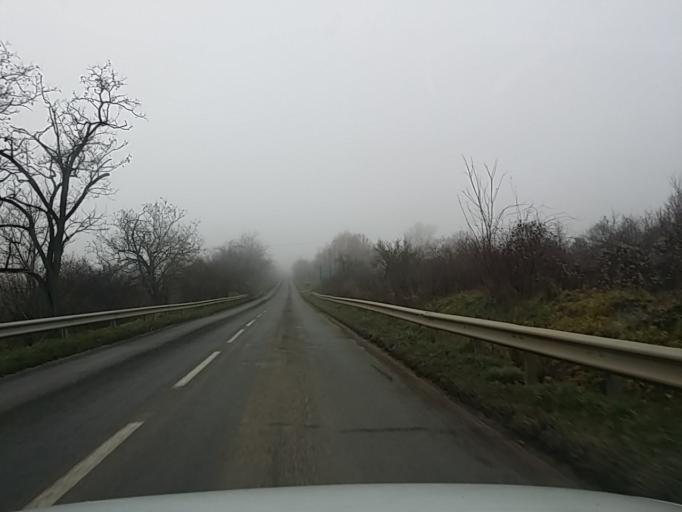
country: HU
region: Pest
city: Budakeszi
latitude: 47.5196
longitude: 18.9107
